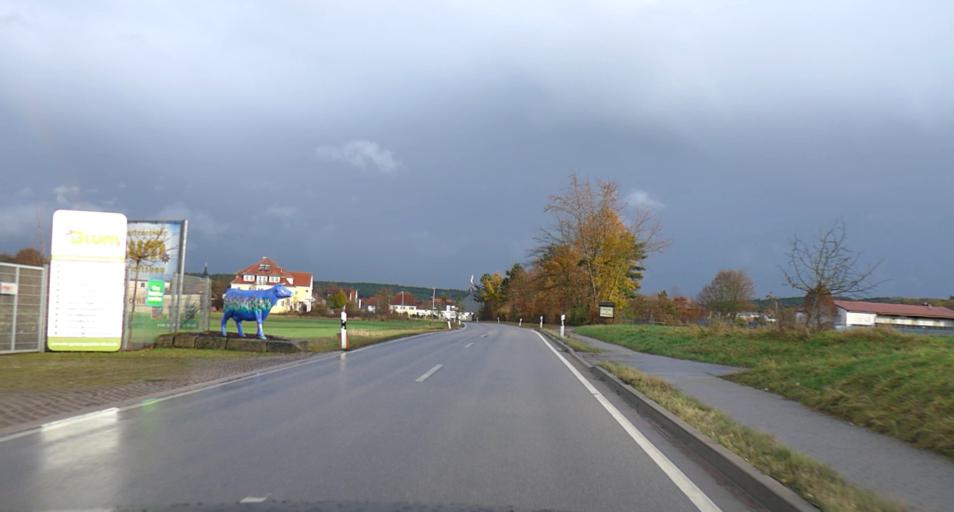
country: DE
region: Bavaria
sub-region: Upper Franconia
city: Langensendelbach
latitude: 49.6415
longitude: 11.0613
